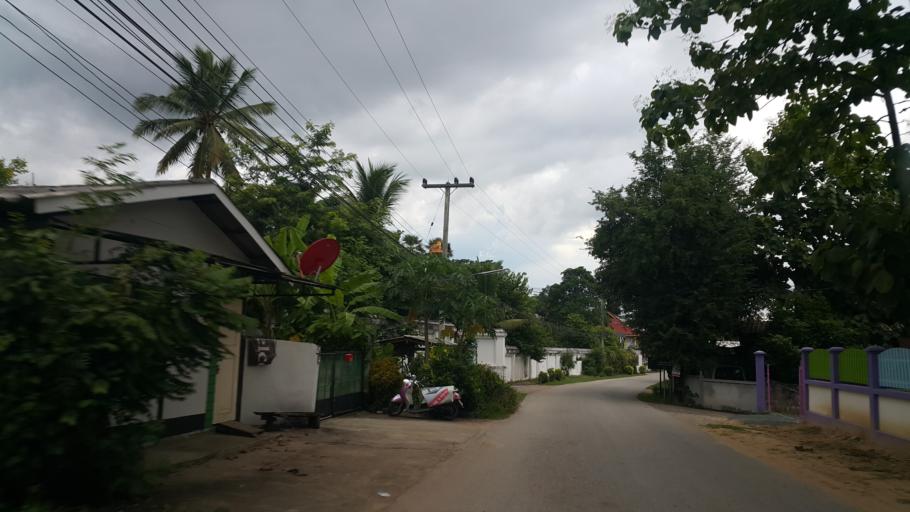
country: TH
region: Chiang Mai
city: Mae On
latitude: 18.7200
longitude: 99.2106
